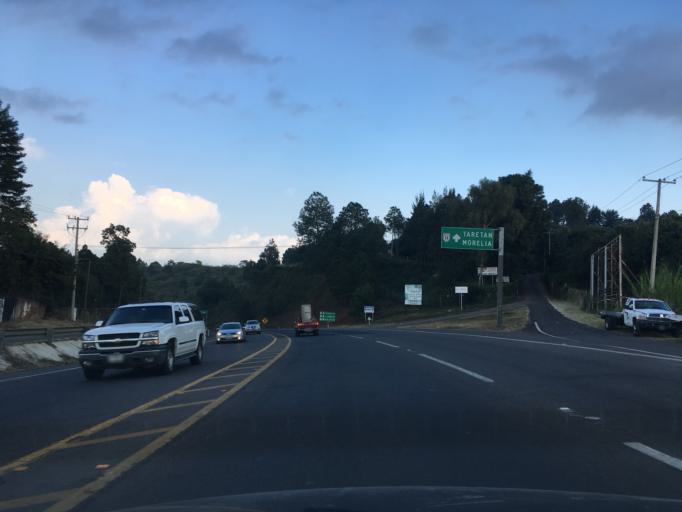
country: MX
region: Michoacan
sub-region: Uruapan
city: Toreo Bajo (El Toreo Bajo)
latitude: 19.4185
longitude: -101.9974
